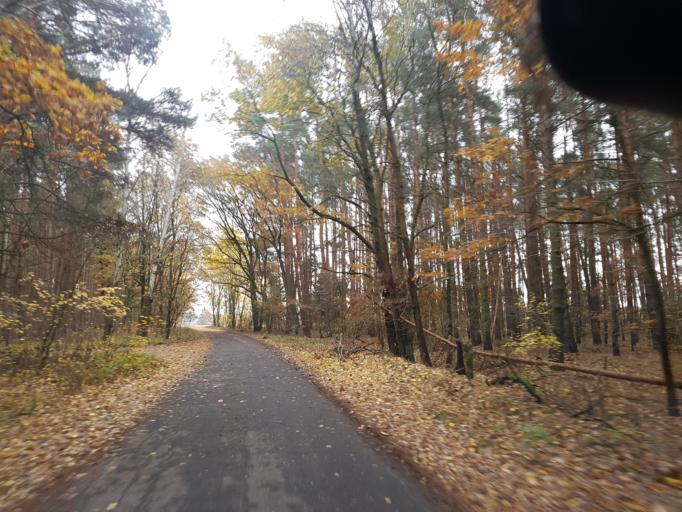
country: DE
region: Brandenburg
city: Treuenbrietzen
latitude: 52.1044
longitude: 12.9183
